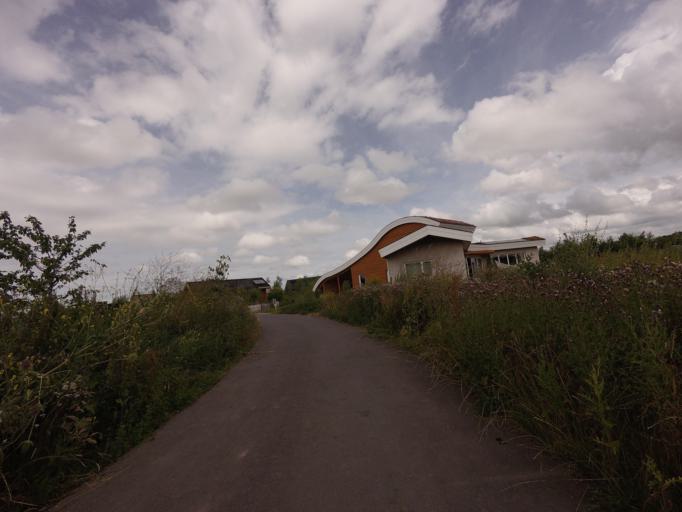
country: NL
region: North Holland
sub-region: Gemeente Huizen
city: Huizen
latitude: 52.3324
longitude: 5.3178
